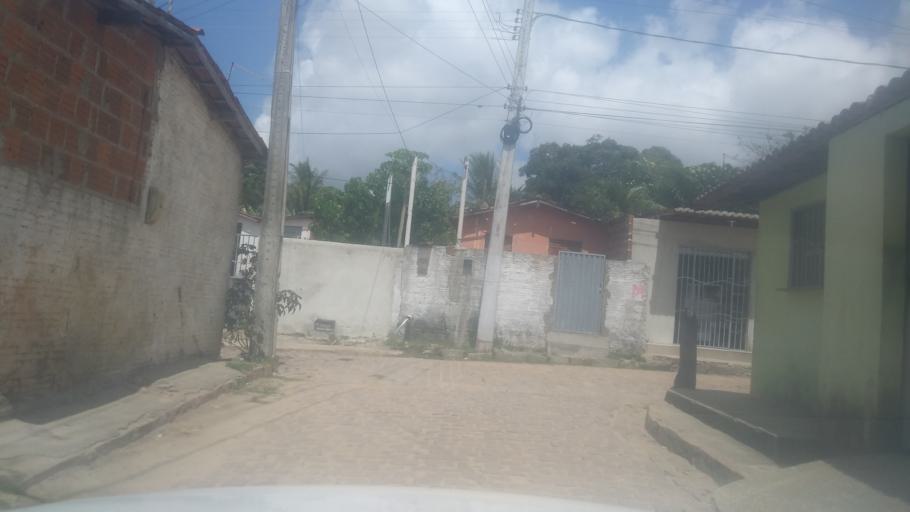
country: BR
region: Rio Grande do Norte
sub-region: Sao Jose De Mipibu
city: Sao Jose de Mipibu
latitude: -6.0707
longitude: -35.2290
